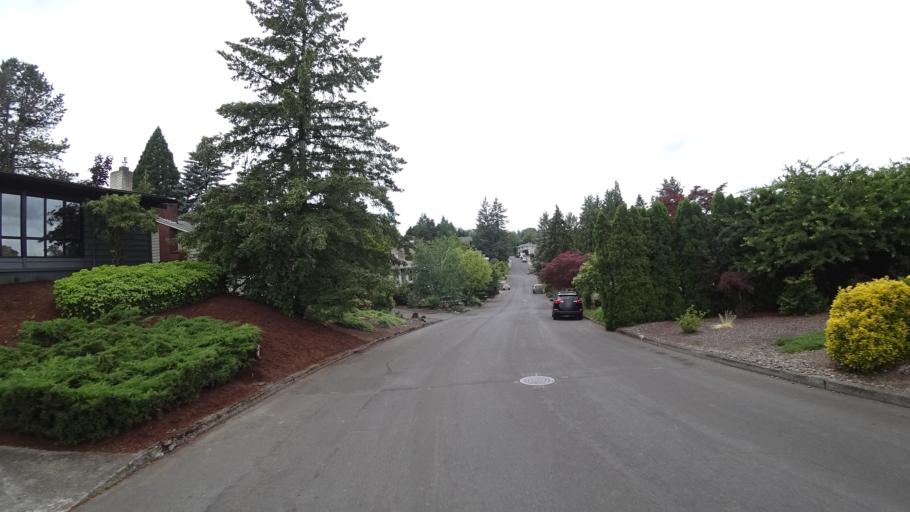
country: US
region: Oregon
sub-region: Clackamas County
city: Lake Oswego
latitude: 45.4549
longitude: -122.7065
